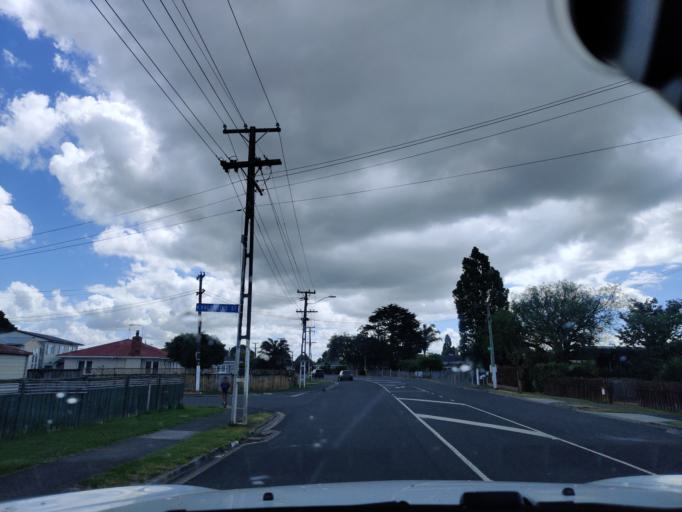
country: NZ
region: Auckland
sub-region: Auckland
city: Red Hill
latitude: -37.0538
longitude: 174.9616
